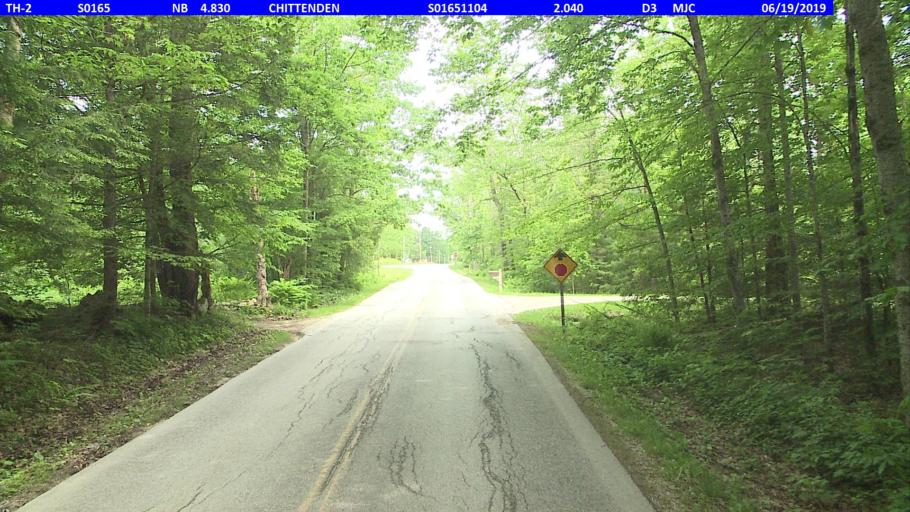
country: US
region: Vermont
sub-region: Rutland County
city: Rutland
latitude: 43.7040
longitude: -72.9603
